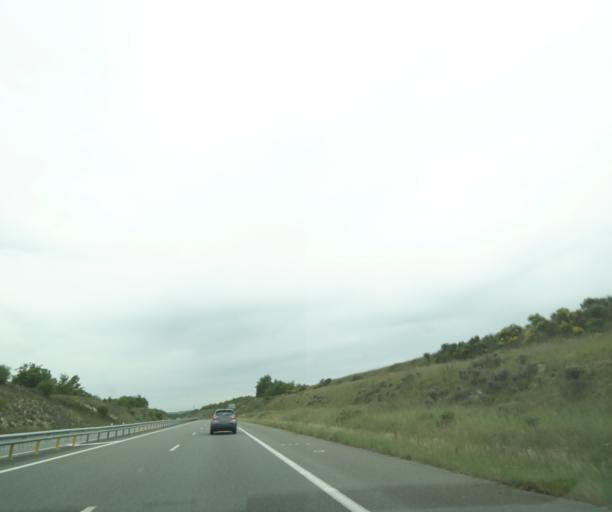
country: FR
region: Midi-Pyrenees
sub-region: Departement du Lot
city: Lalbenque
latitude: 44.3471
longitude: 1.4995
